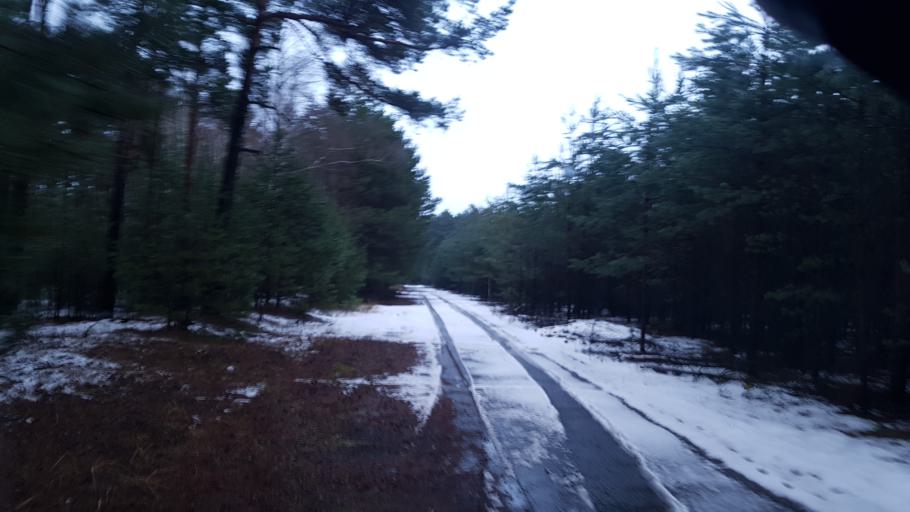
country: DE
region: Brandenburg
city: Janschwalde
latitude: 51.8848
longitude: 14.5434
